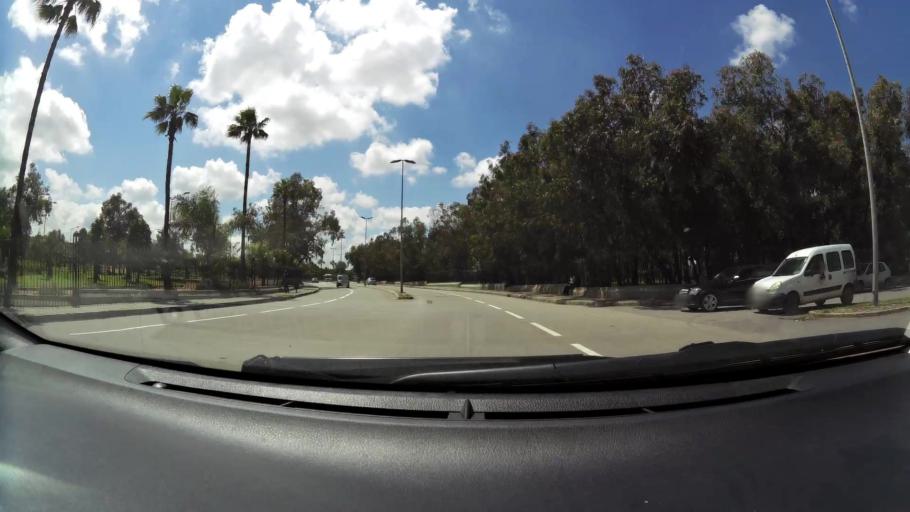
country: MA
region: Grand Casablanca
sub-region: Casablanca
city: Casablanca
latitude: 33.5562
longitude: -7.5662
